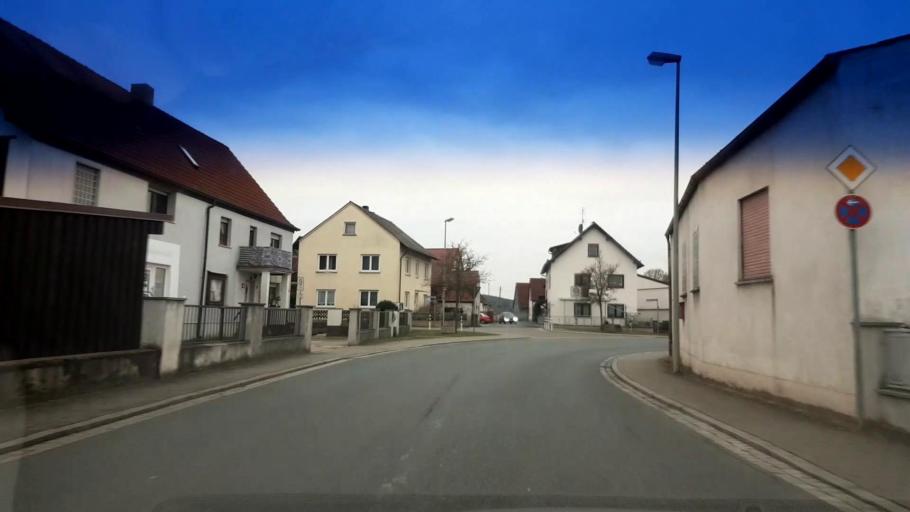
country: DE
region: Bavaria
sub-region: Upper Franconia
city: Pettstadt
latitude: 49.7999
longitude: 10.9278
